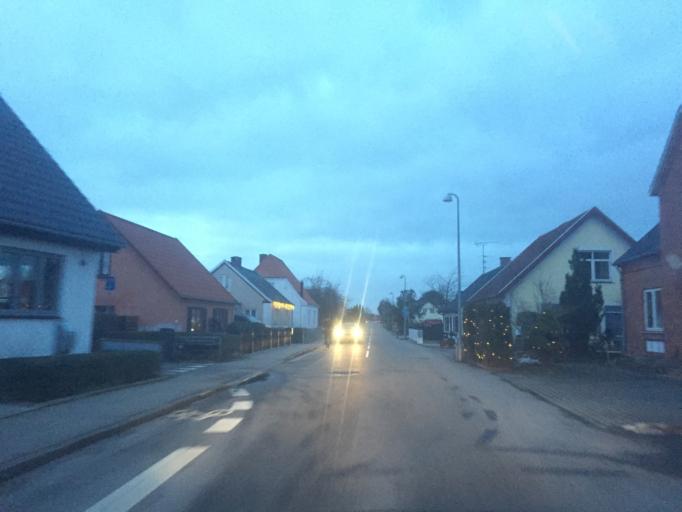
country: DK
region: Capital Region
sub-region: Hoje-Taastrup Kommune
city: Flong
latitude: 55.6450
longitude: 12.1951
